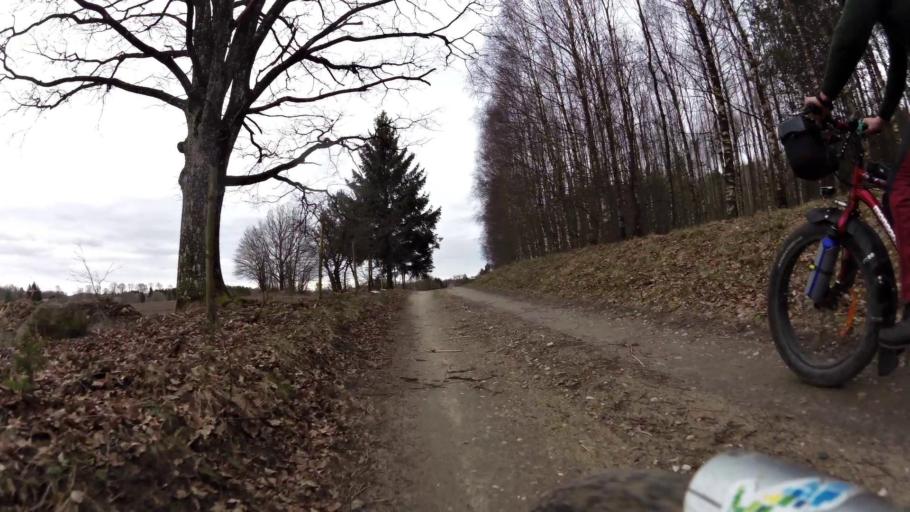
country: PL
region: Pomeranian Voivodeship
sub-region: Powiat bytowski
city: Trzebielino
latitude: 54.1098
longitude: 17.1302
